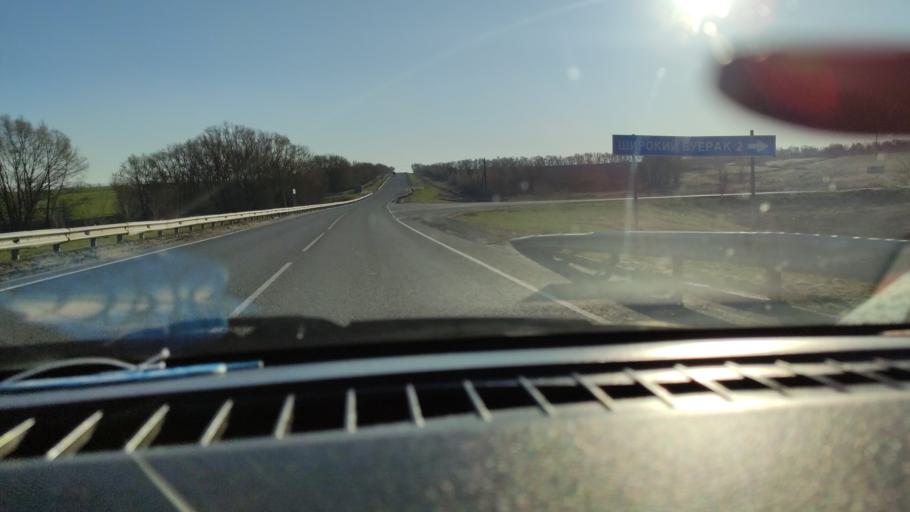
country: RU
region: Saratov
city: Balakovo
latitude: 52.1303
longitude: 47.7636
